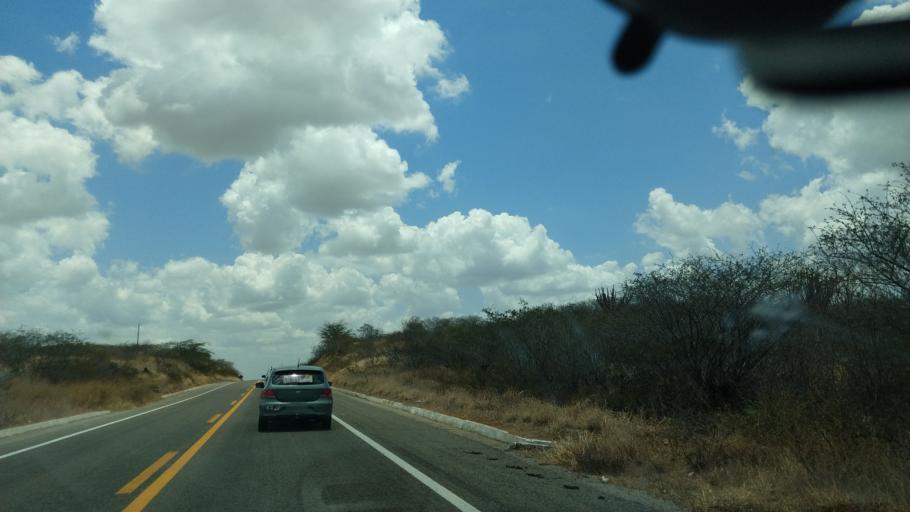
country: BR
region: Rio Grande do Norte
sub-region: Cerro Cora
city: Cerro Cora
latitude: -6.2088
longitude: -36.2910
